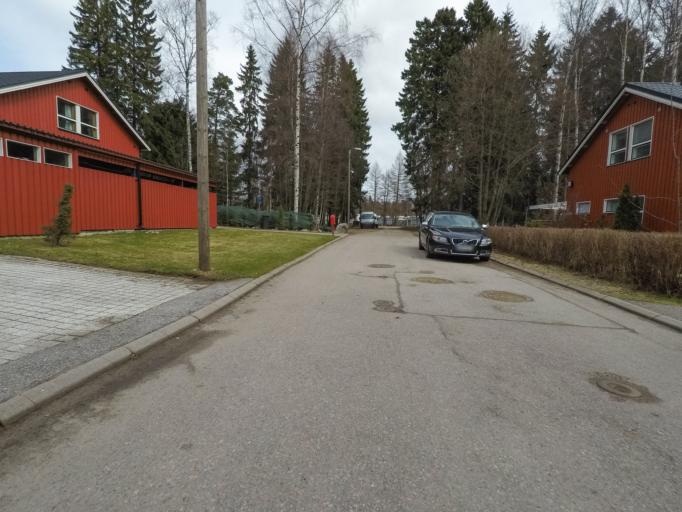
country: FI
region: Uusimaa
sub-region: Helsinki
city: Vantaa
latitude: 60.2245
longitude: 25.0527
